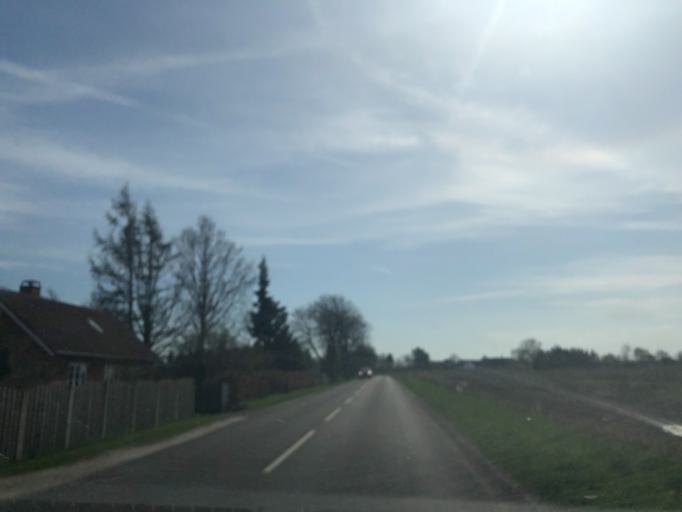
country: DK
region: Zealand
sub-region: Faxe Kommune
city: Ronnede
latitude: 55.2946
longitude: 12.0703
